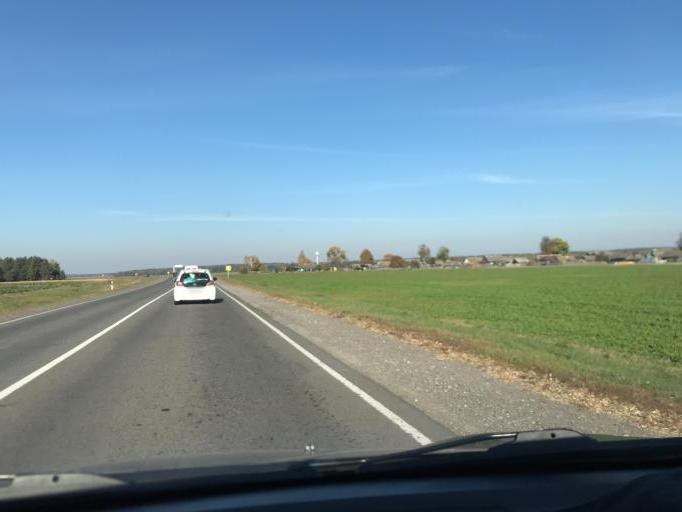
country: BY
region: Gomel
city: Parychy
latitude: 52.6364
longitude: 29.3775
